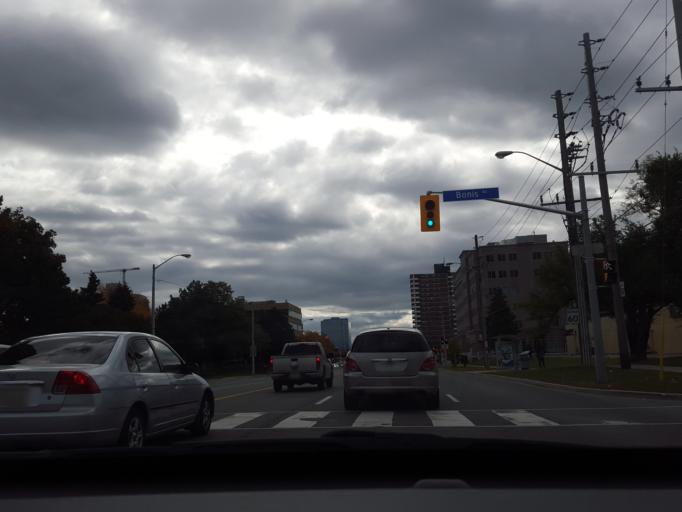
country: CA
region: Ontario
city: Scarborough
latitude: 43.7859
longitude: -79.2894
